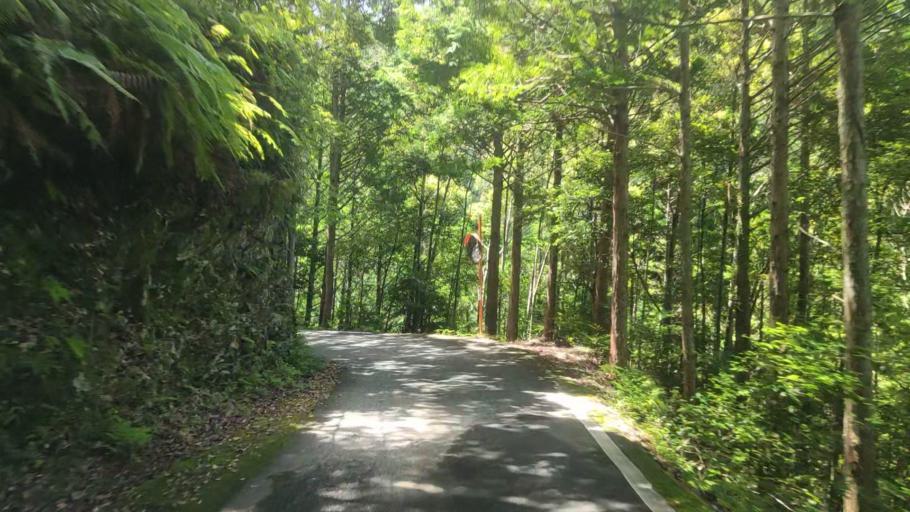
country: JP
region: Wakayama
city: Shingu
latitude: 33.9080
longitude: 135.8639
